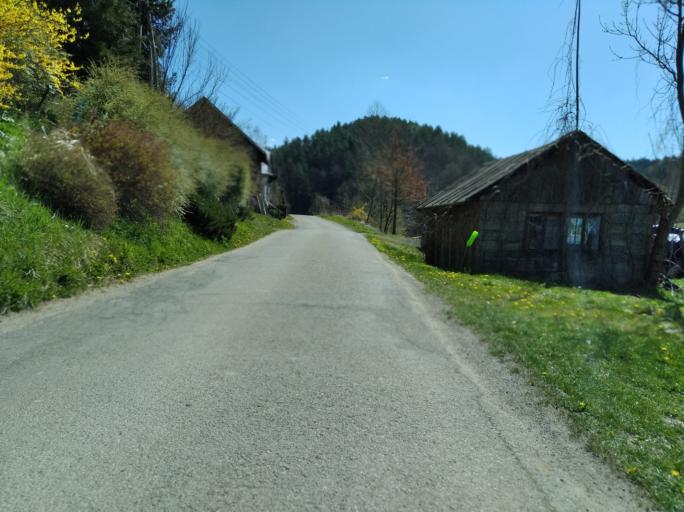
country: PL
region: Subcarpathian Voivodeship
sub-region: Powiat brzozowski
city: Dydnia
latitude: 49.7138
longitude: 22.1750
